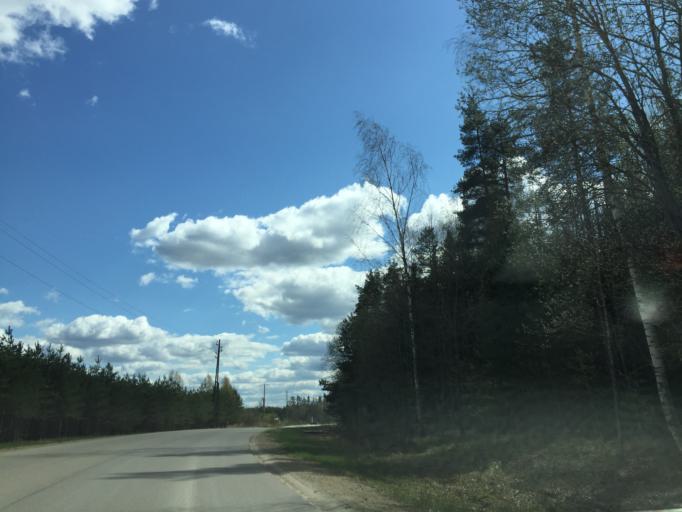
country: LV
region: Vilanu
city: Vilani
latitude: 56.5635
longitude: 27.0538
